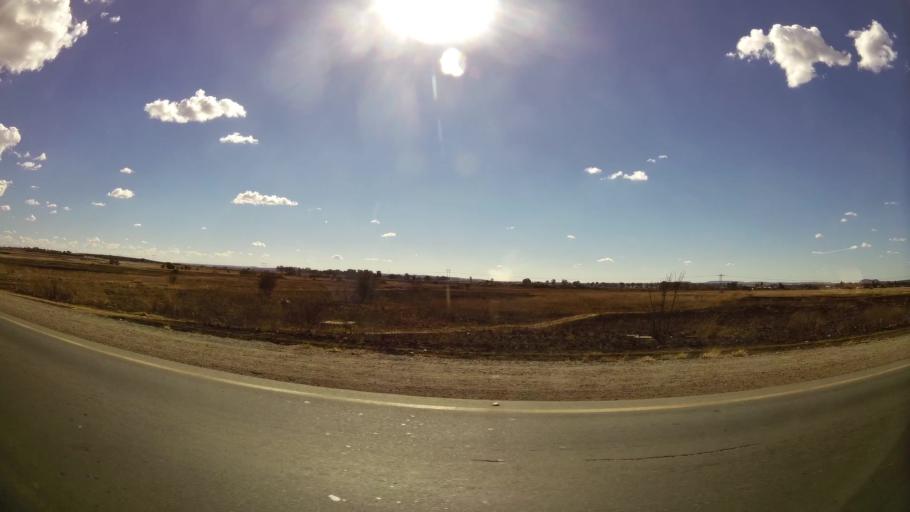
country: ZA
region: North-West
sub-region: Dr Kenneth Kaunda District Municipality
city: Klerksdorp
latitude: -26.8713
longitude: 26.6126
